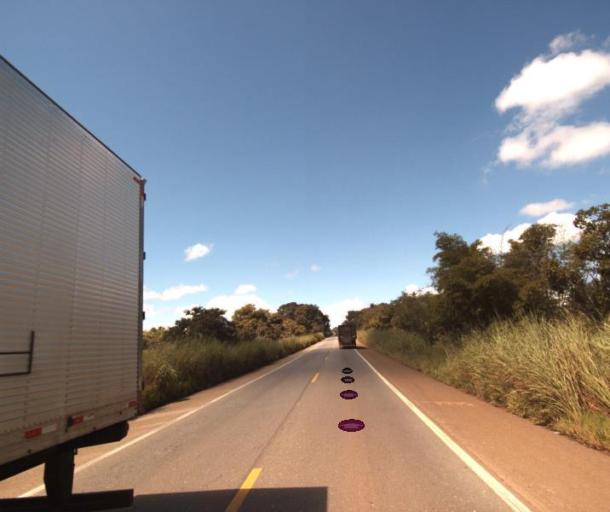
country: BR
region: Goias
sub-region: Jaragua
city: Jaragua
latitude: -15.7185
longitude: -49.3291
